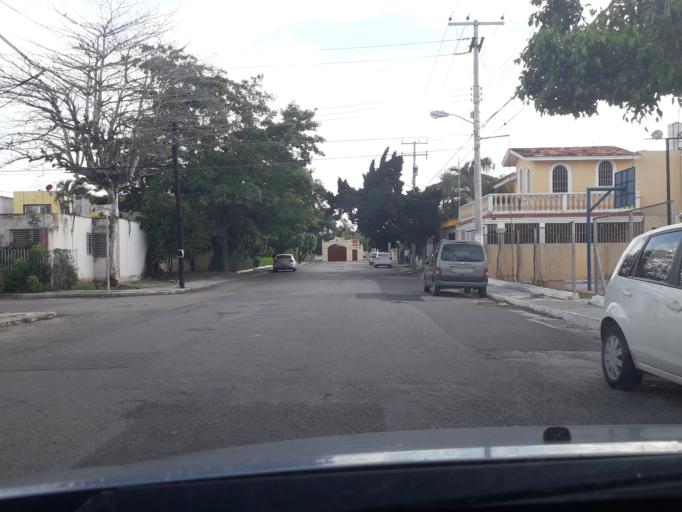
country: MX
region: Yucatan
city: Merida
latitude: 21.0074
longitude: -89.6394
